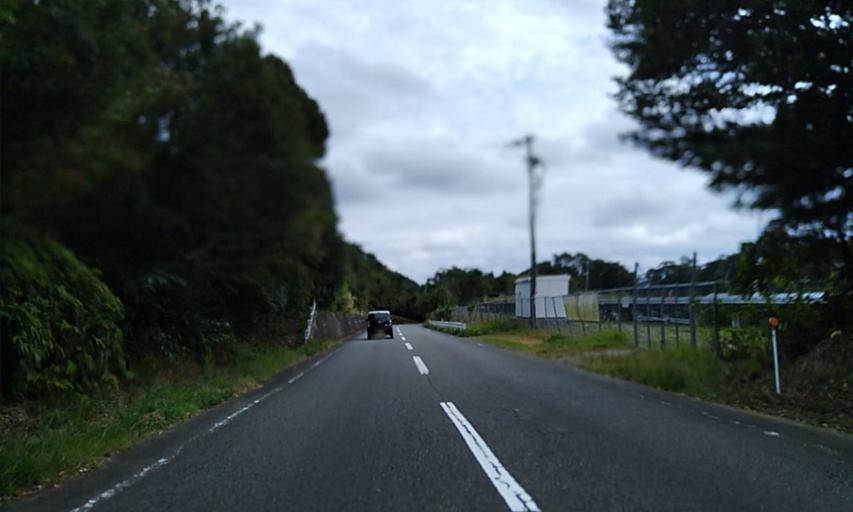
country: JP
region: Wakayama
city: Shingu
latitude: 33.4697
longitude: 135.8413
